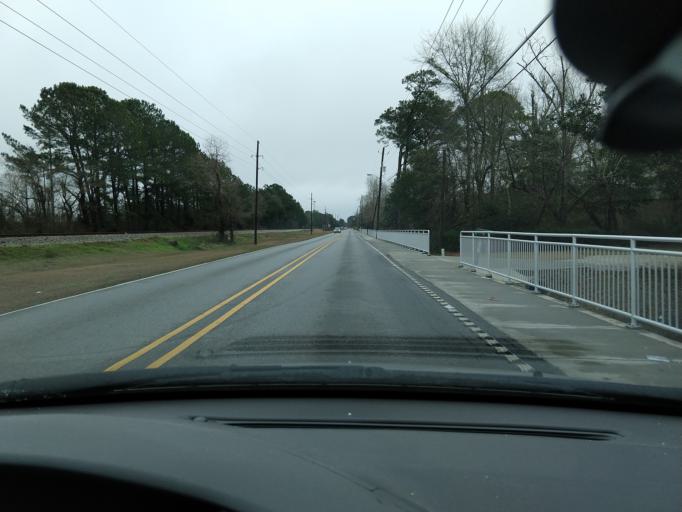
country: US
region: Mississippi
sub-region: Jackson County
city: Ocean Springs
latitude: 30.4115
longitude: -88.7930
